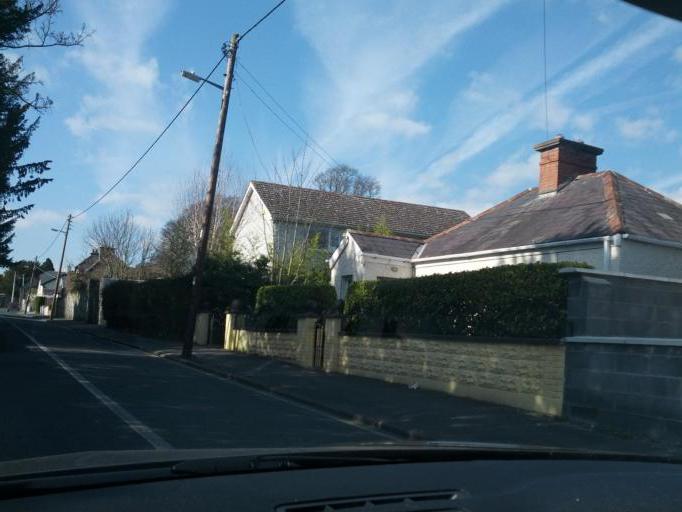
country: IE
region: Leinster
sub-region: Kildare
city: Celbridge
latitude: 53.3380
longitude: -6.5436
